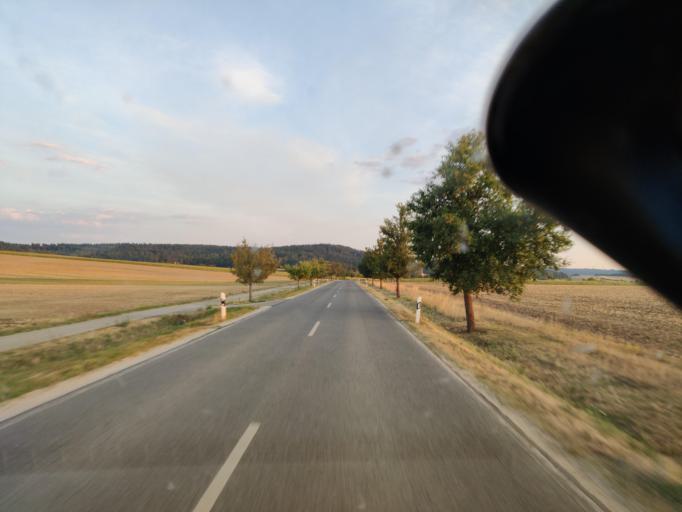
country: DE
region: Bavaria
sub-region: Regierungsbezirk Mittelfranken
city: Thalmassing
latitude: 49.1402
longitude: 11.2133
